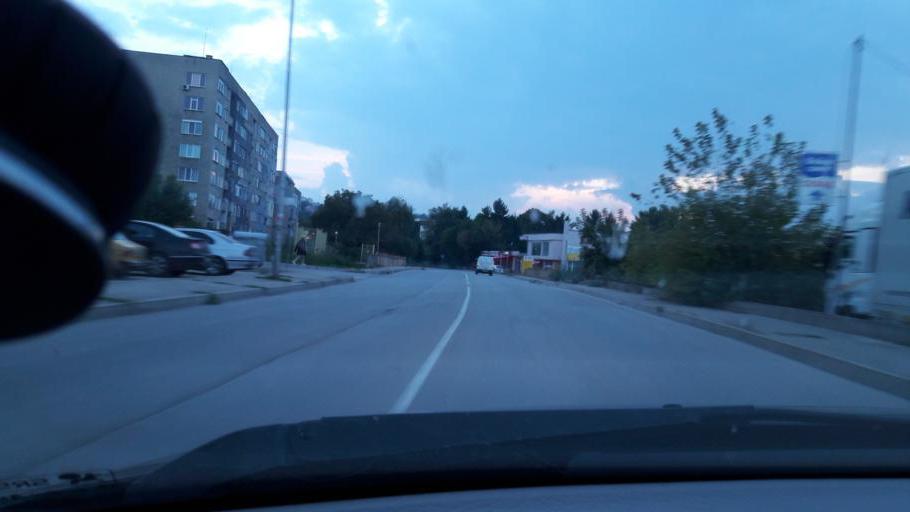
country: BG
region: Razgrad
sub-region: Obshtina Razgrad
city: Razgrad
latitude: 43.5327
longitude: 26.5162
